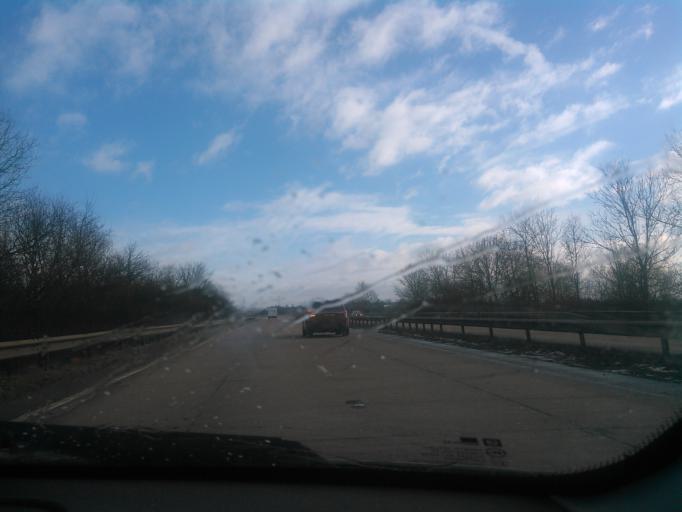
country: GB
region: England
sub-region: Staffordshire
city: Cheadle
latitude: 52.9541
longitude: -2.0302
